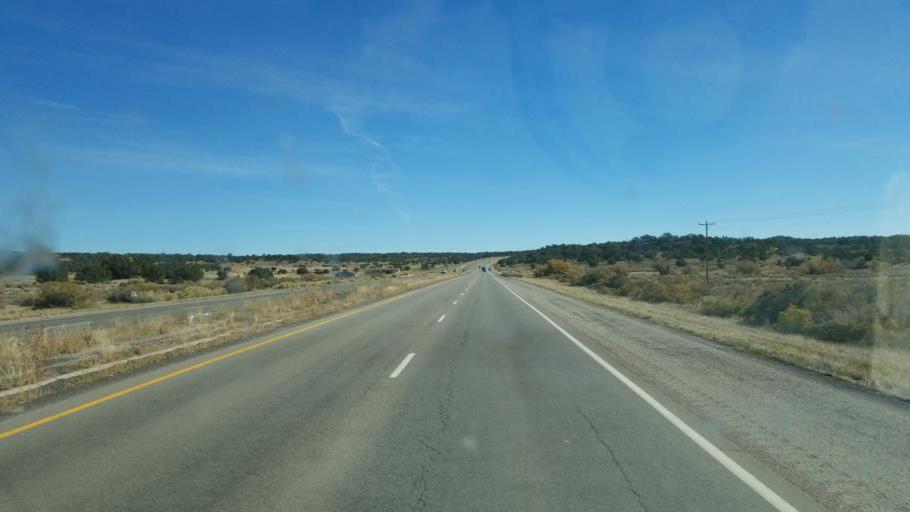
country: US
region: New Mexico
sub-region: McKinley County
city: Twin Lakes
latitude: 35.6339
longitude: -108.8925
